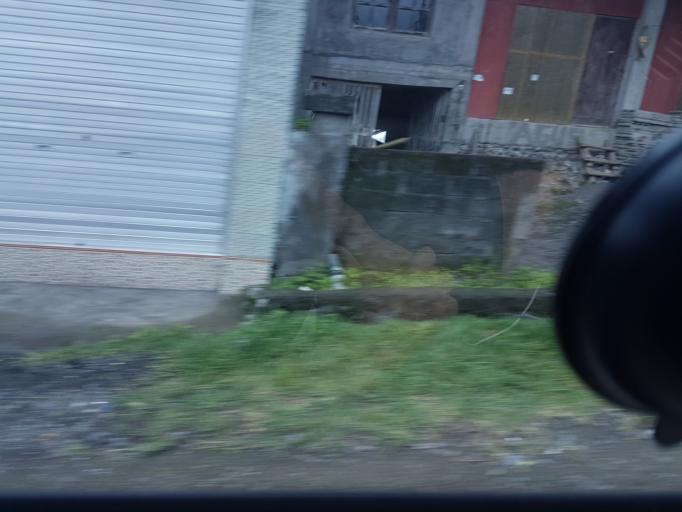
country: ID
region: Bali
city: Banjar Kedisan
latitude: -8.3022
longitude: 115.3543
